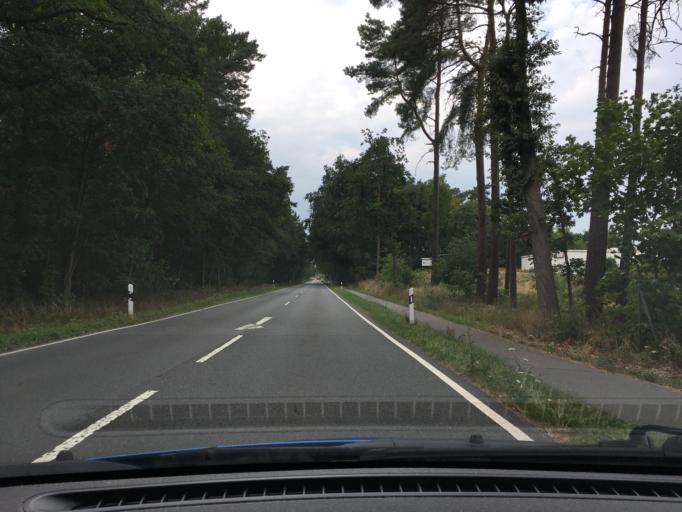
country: DE
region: Lower Saxony
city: Adelheidsdorf
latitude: 52.5622
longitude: 10.0675
